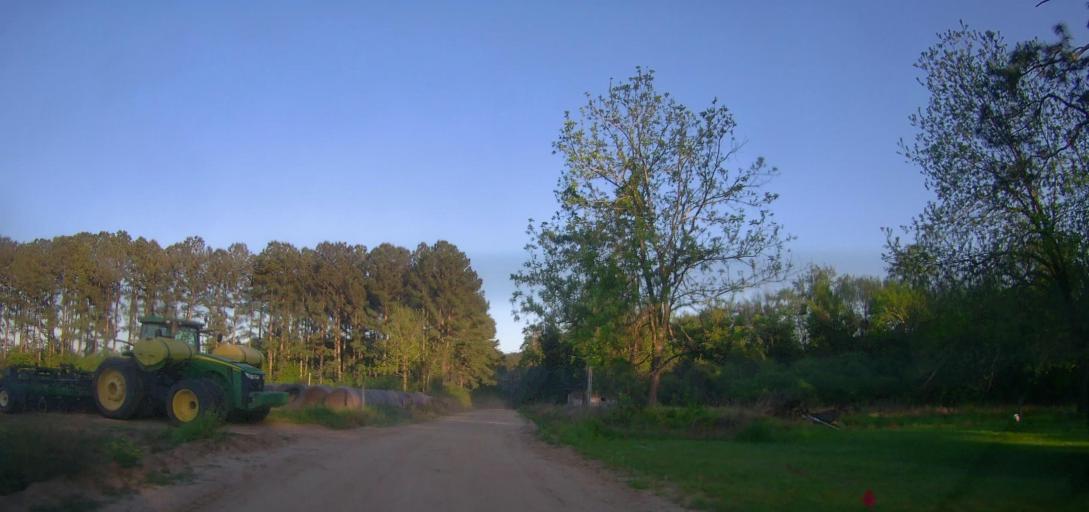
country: US
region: Georgia
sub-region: Irwin County
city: Ocilla
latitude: 31.6503
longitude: -83.2286
